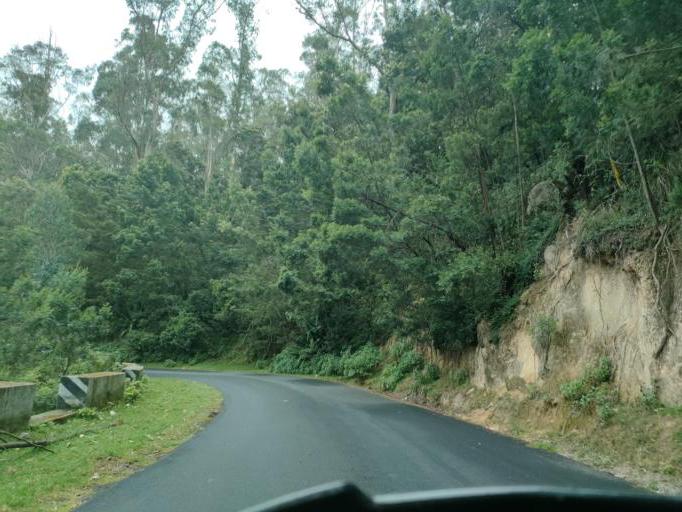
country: IN
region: Tamil Nadu
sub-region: Dindigul
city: Kodaikanal
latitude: 10.2402
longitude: 77.3663
